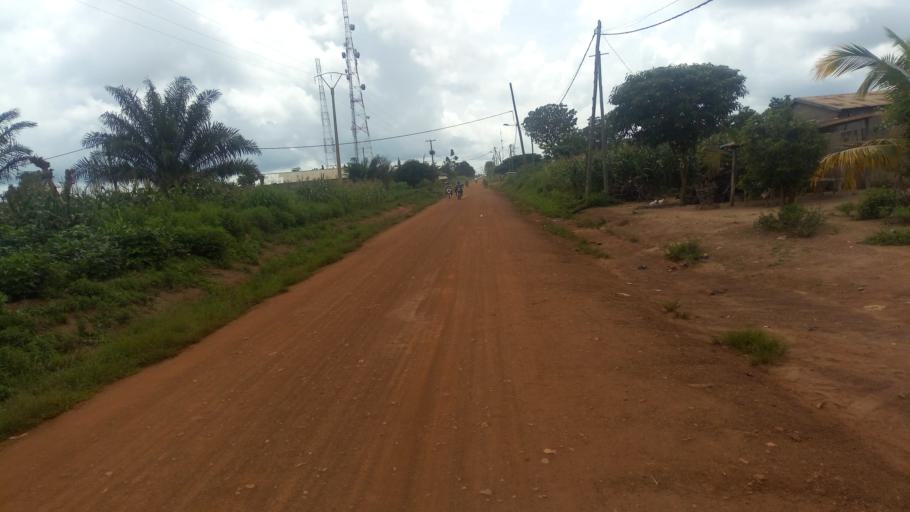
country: TG
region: Centrale
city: Sotouboua
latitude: 8.5559
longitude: 1.0012
